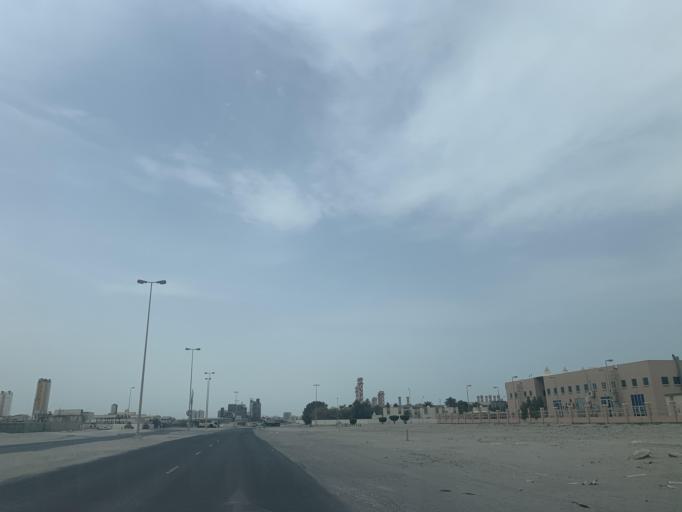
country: BH
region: Muharraq
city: Al Hadd
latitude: 26.2090
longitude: 50.6589
